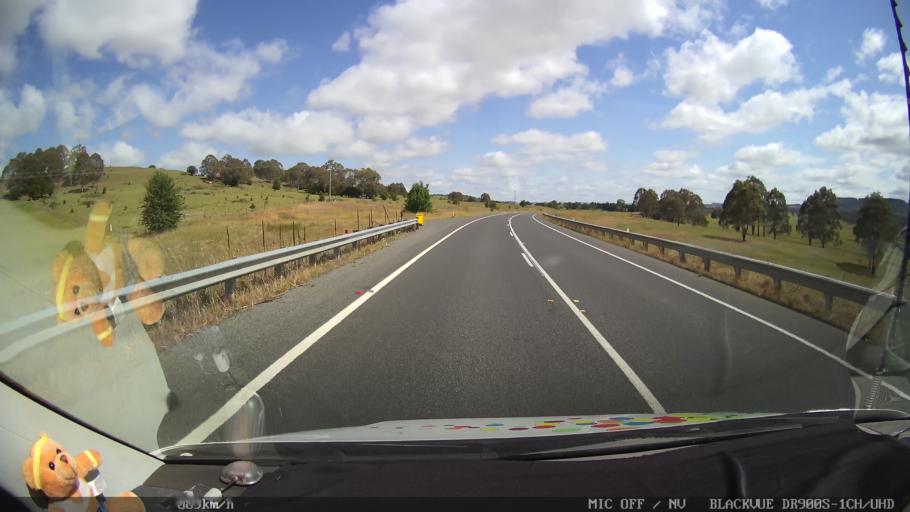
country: AU
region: New South Wales
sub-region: Glen Innes Severn
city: Glen Innes
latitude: -29.8900
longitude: 151.7330
